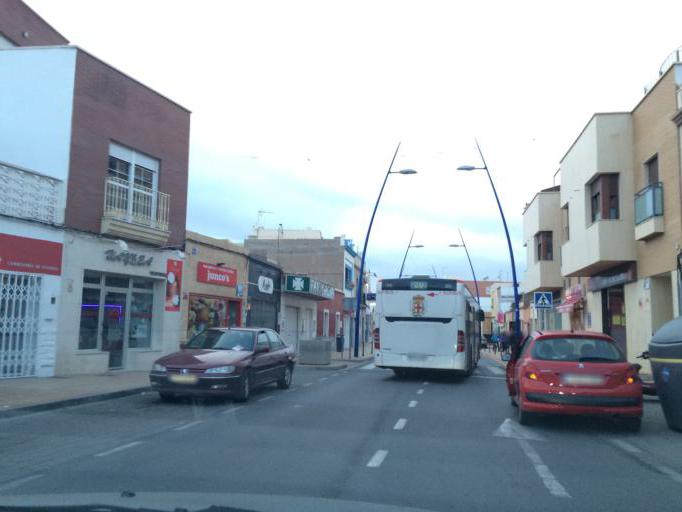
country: ES
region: Andalusia
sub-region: Provincia de Almeria
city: Almeria
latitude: 36.8407
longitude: -2.4091
